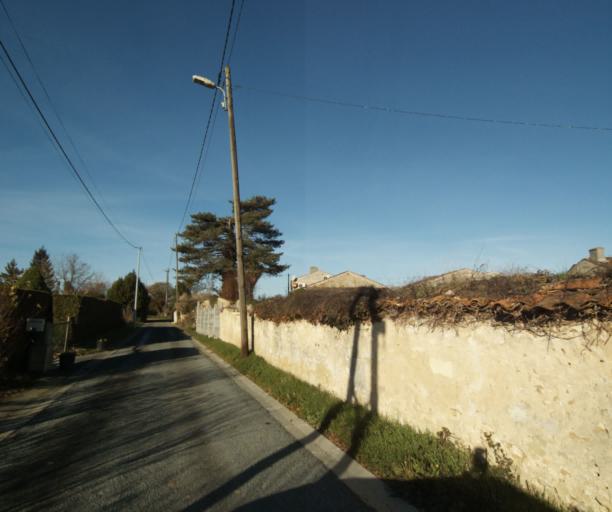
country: FR
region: Poitou-Charentes
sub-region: Departement de la Charente-Maritime
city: Cherac
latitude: 45.7356
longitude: -0.4254
